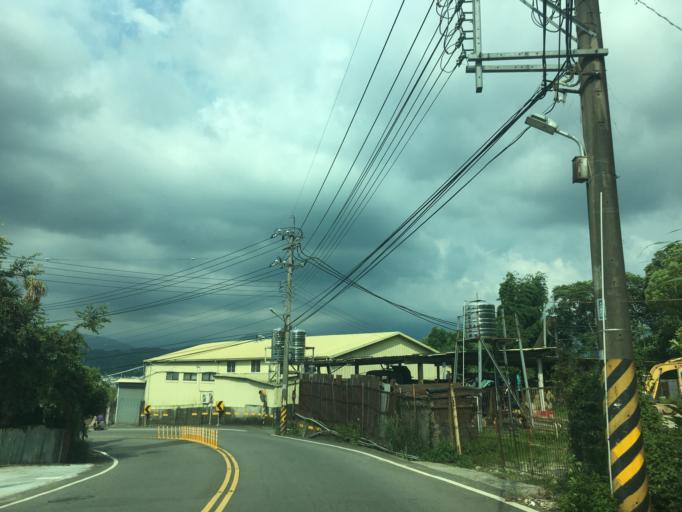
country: TW
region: Taiwan
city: Fengyuan
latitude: 24.2534
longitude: 120.8140
